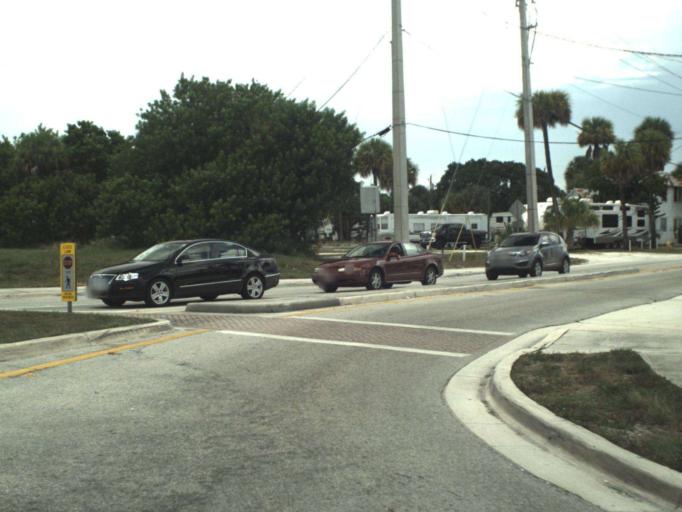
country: US
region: Florida
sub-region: Martin County
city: Jensen Beach
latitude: 27.2508
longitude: -80.2279
